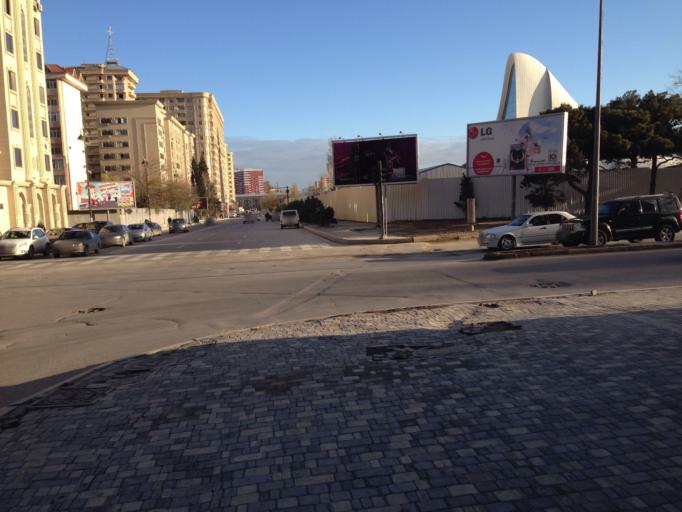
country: AZ
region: Baki
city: Baku
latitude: 40.3996
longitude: 49.8661
